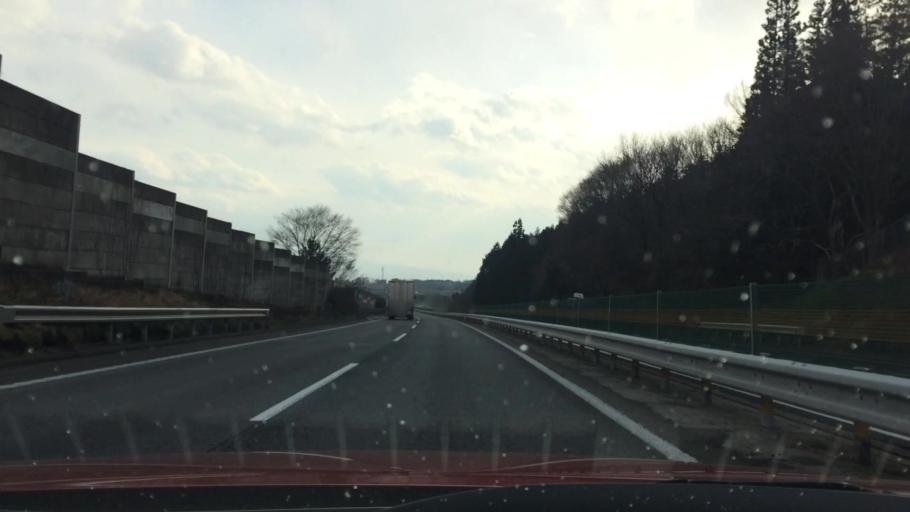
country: JP
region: Nagano
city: Ina
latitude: 35.6887
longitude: 137.9093
